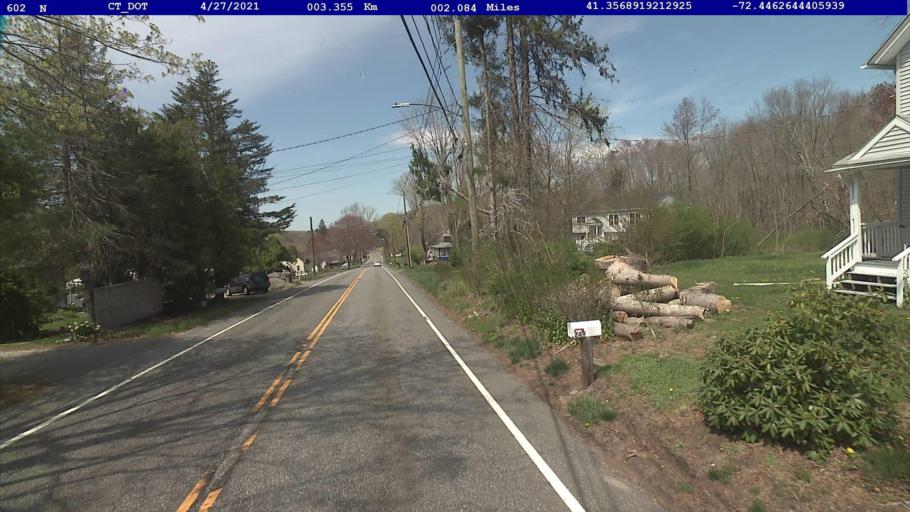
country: US
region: Connecticut
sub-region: Middlesex County
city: Deep River Center
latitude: 41.3568
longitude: -72.4462
